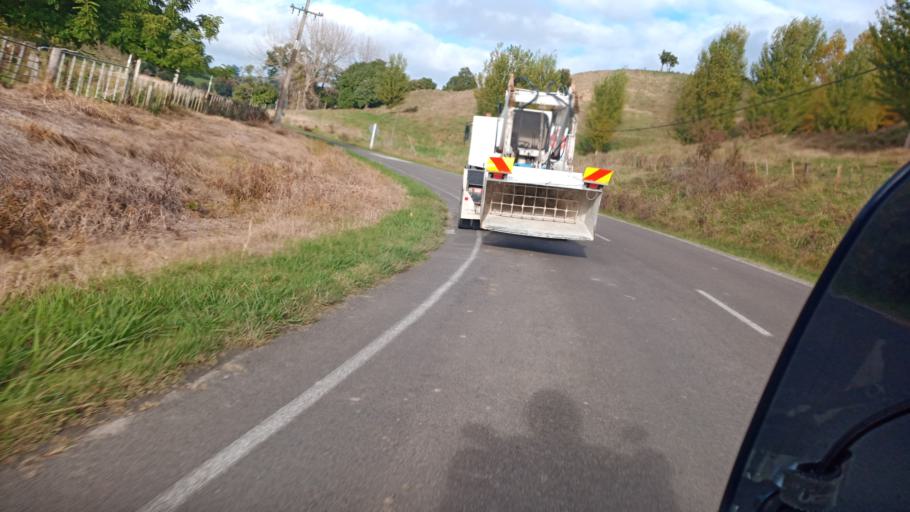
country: NZ
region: Gisborne
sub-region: Gisborne District
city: Gisborne
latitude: -38.5855
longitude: 177.7865
